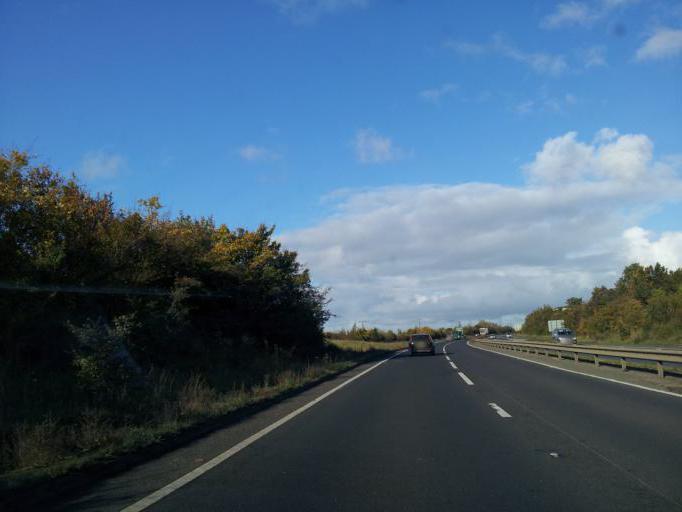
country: GB
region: England
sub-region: Norfolk
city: King's Lynn
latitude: 52.7367
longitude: 0.3931
